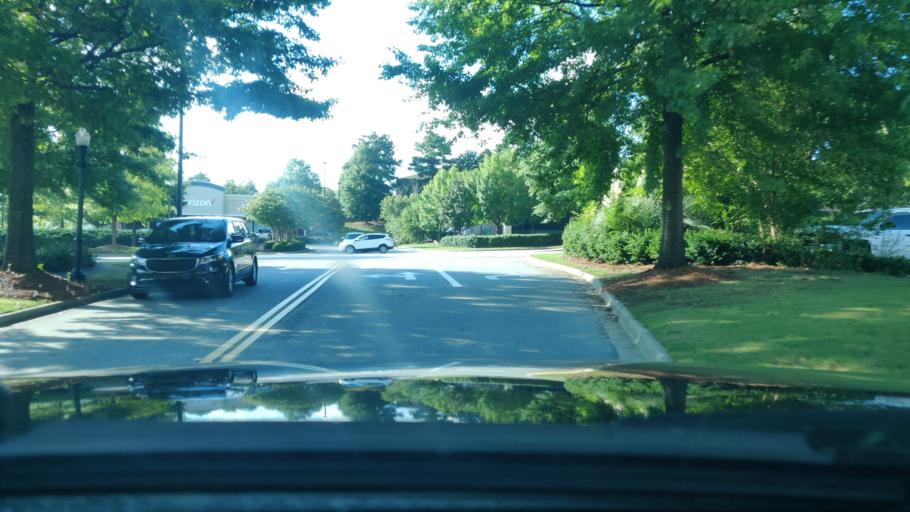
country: US
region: Alabama
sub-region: Lee County
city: Opelika
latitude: 32.6195
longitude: -85.4052
